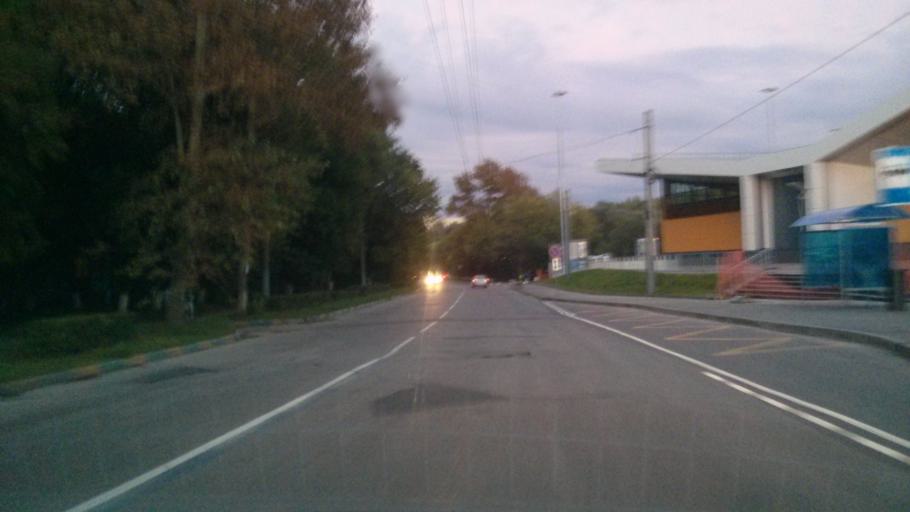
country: RU
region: Nizjnij Novgorod
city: Nizhniy Novgorod
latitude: 56.2967
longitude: 44.0459
